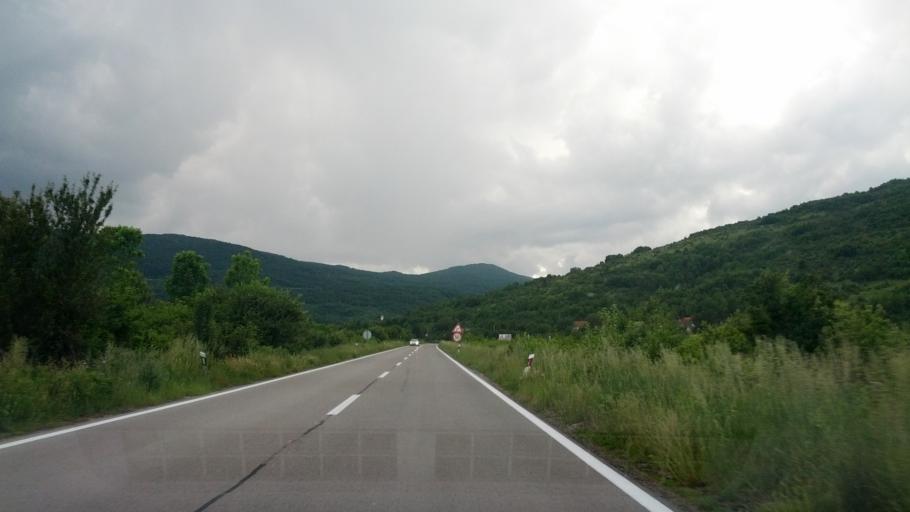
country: BA
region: Federation of Bosnia and Herzegovina
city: Izacic
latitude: 44.8795
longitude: 15.7308
